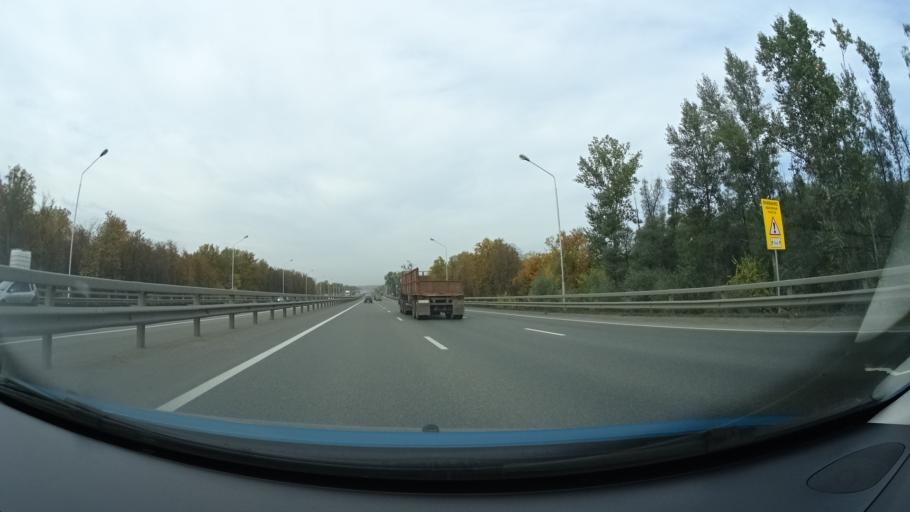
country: RU
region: Bashkortostan
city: Ufa
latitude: 54.6629
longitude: 55.8711
